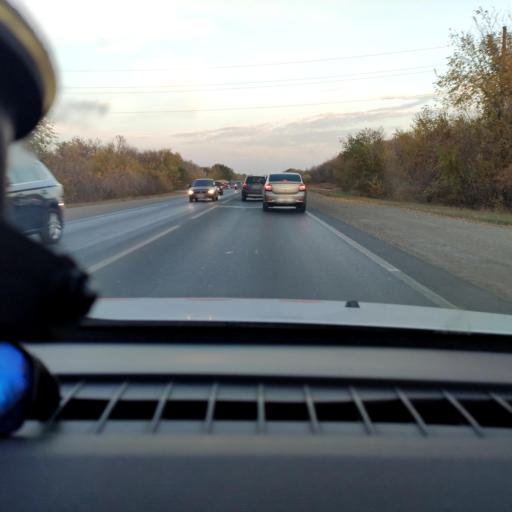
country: RU
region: Samara
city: Samara
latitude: 53.0808
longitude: 50.0974
